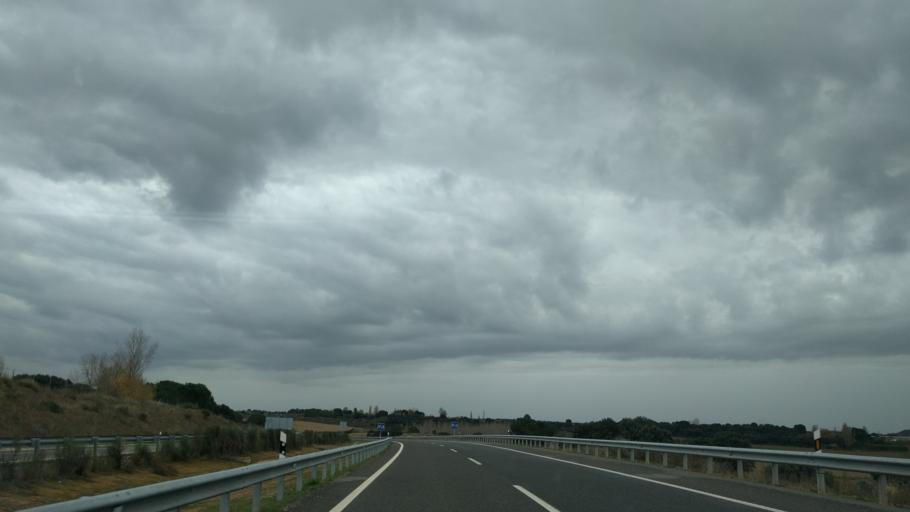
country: ES
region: Aragon
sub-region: Provincia de Huesca
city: Monzon
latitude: 41.9434
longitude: 0.1947
